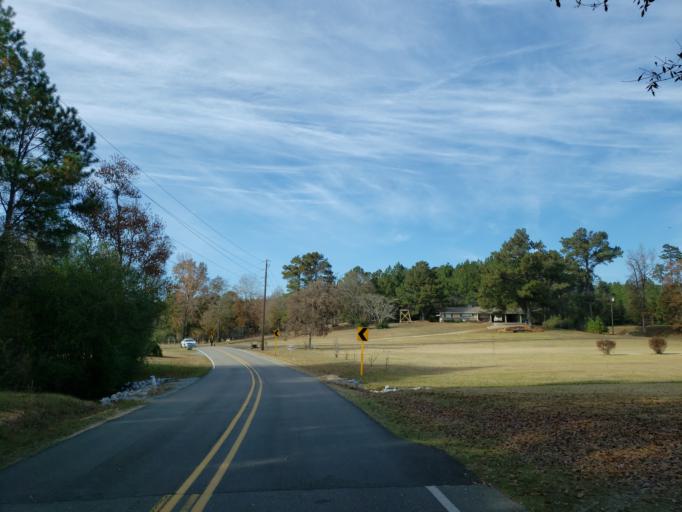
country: US
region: Mississippi
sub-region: Forrest County
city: Rawls Springs
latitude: 31.3995
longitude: -89.3622
